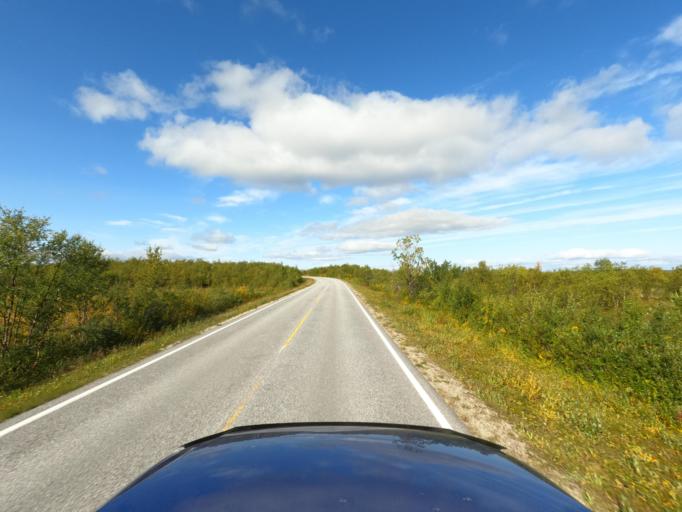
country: NO
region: Finnmark Fylke
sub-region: Karasjok
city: Karasjohka
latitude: 69.6071
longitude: 25.3216
